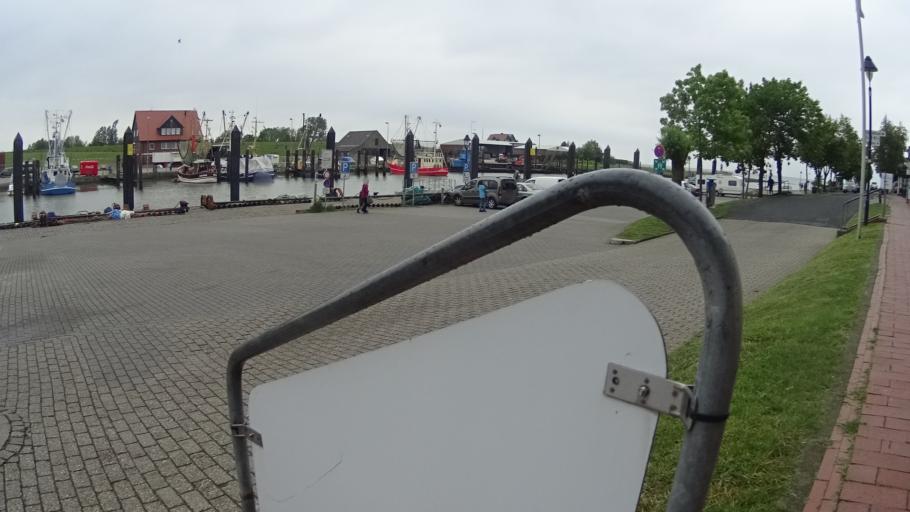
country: DE
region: Lower Saxony
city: Butjadingen
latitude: 53.5968
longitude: 8.3555
